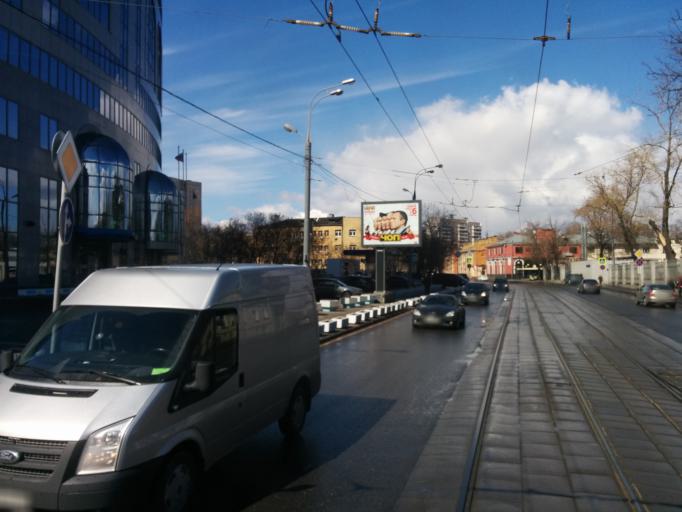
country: RU
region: Moscow
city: Sokol'niki
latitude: 55.7766
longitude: 37.6489
